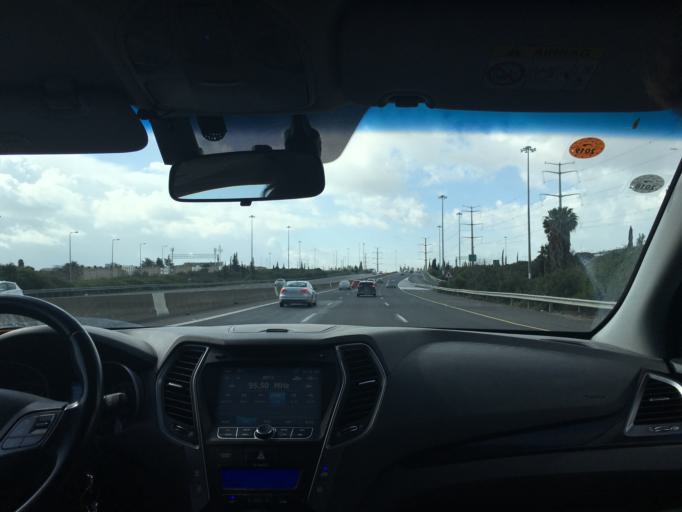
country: IL
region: Tel Aviv
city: Azor
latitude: 32.0158
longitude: 34.8195
